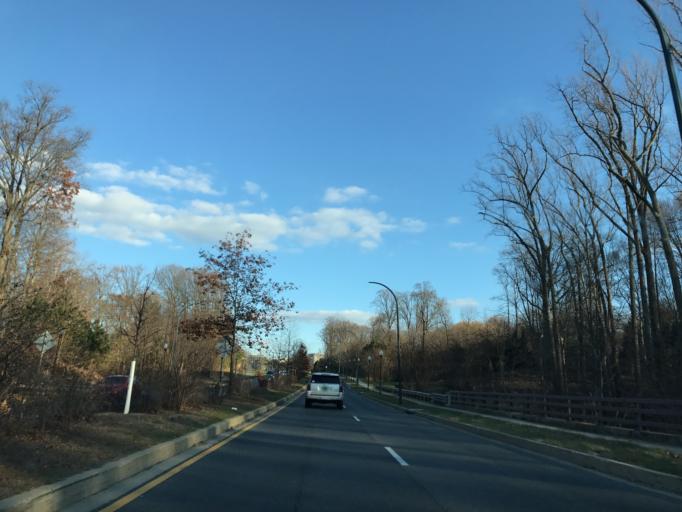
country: US
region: Maryland
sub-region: Montgomery County
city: North Bethesda
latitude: 39.0512
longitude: -77.1335
